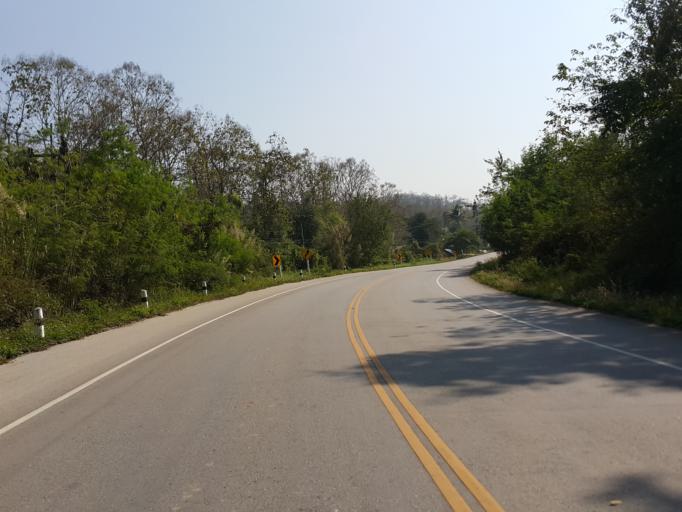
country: TH
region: Lampang
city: Mueang Pan
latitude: 18.8436
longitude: 99.6024
